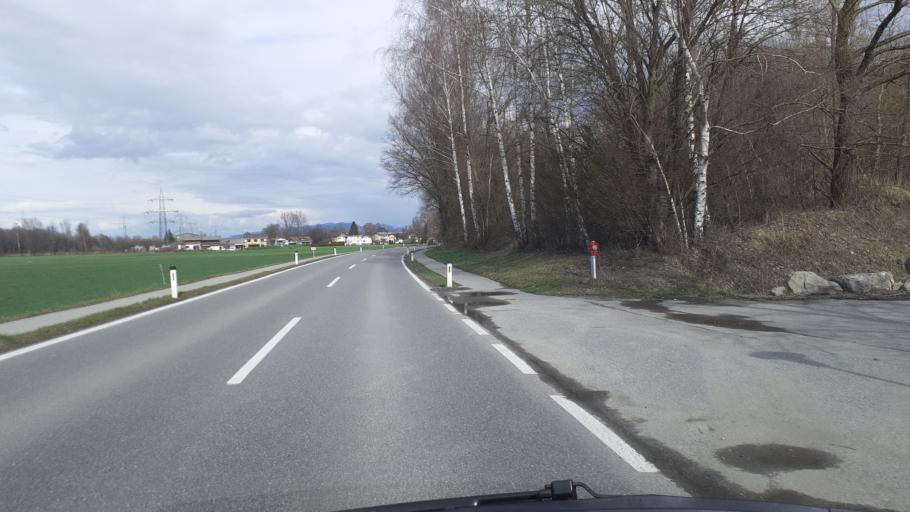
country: AT
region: Vorarlberg
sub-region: Politischer Bezirk Feldkirch
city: Koblach
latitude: 47.3419
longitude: 9.6031
